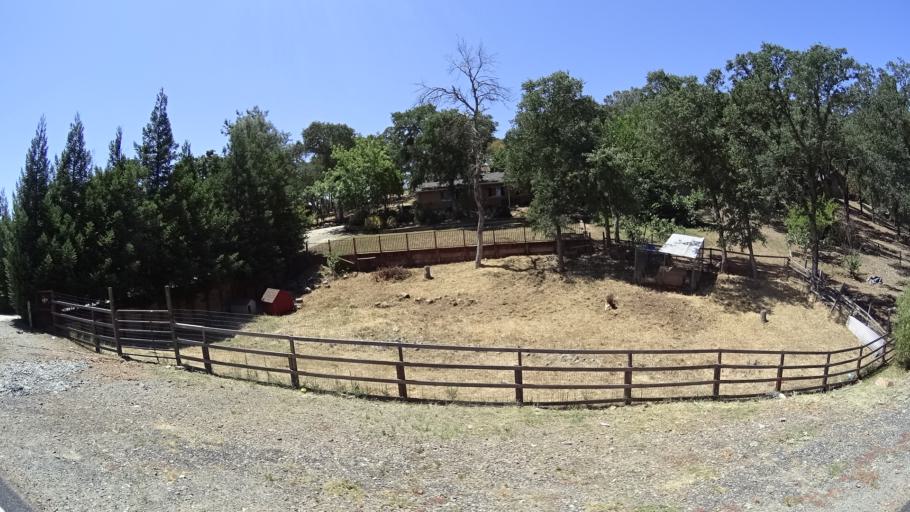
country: US
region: California
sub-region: Calaveras County
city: Rancho Calaveras
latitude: 38.1296
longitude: -120.8697
